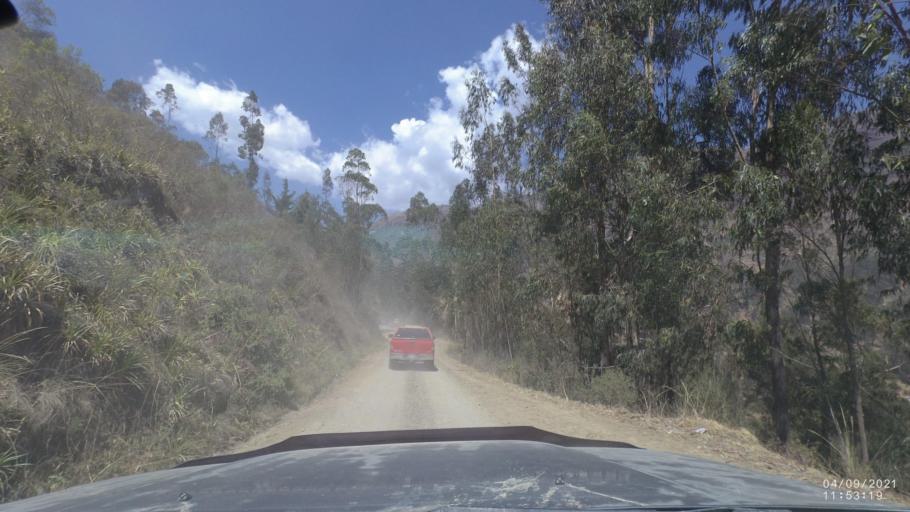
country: BO
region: Cochabamba
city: Colchani
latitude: -17.2336
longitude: -66.5262
